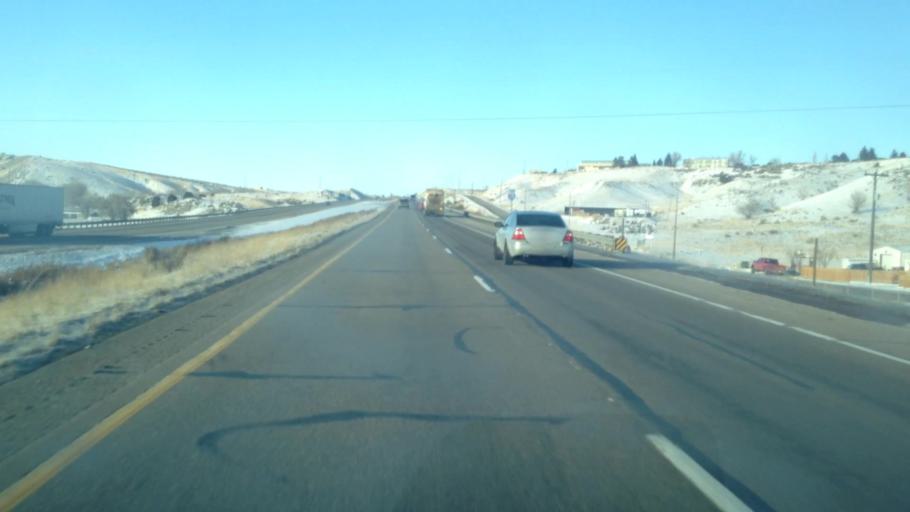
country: US
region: Idaho
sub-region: Bannock County
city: Pocatello
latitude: 42.8449
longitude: -112.4126
